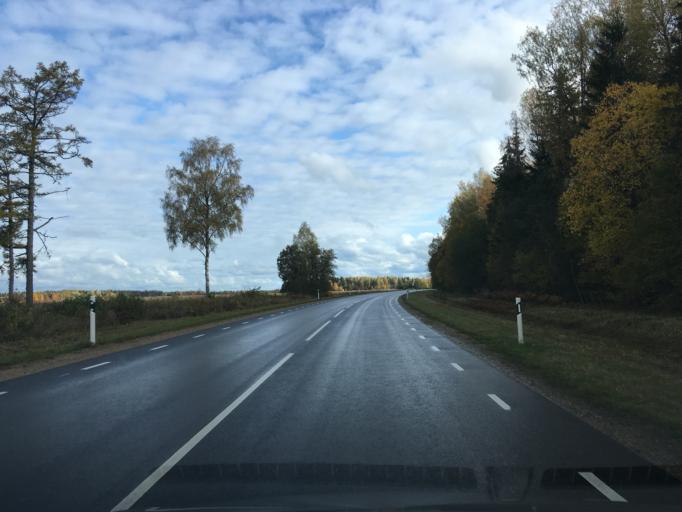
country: EE
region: Harju
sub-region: Raasiku vald
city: Raasiku
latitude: 59.2091
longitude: 25.1900
